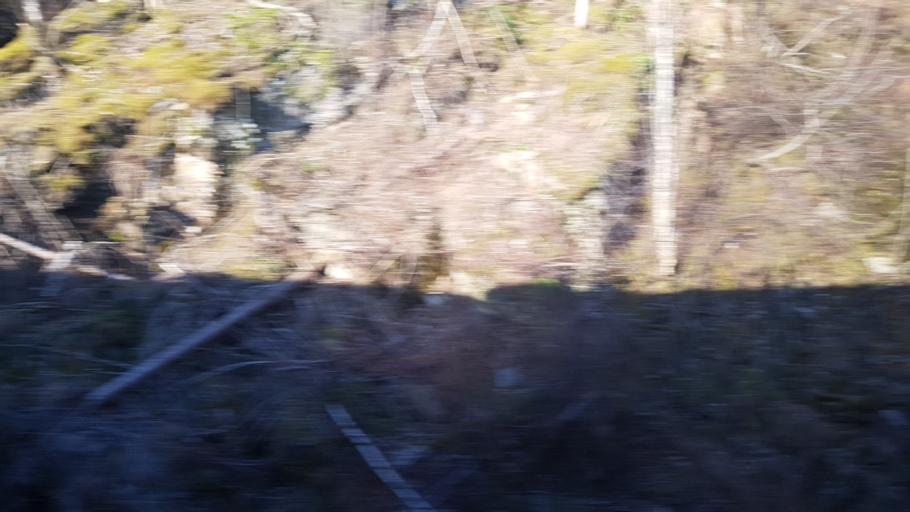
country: NO
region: Sor-Trondelag
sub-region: Malvik
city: Hommelvik
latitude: 63.4142
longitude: 10.7897
